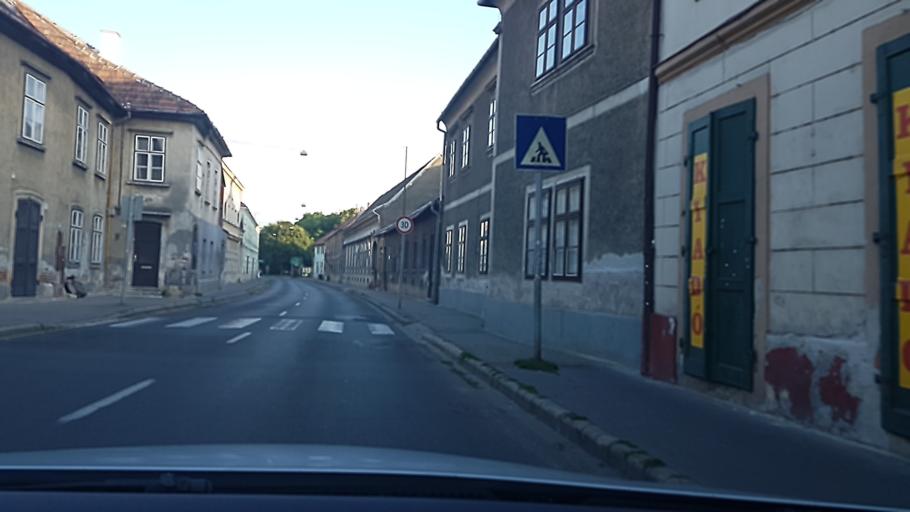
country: HU
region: Gyor-Moson-Sopron
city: Sopron
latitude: 47.6812
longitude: 16.5938
